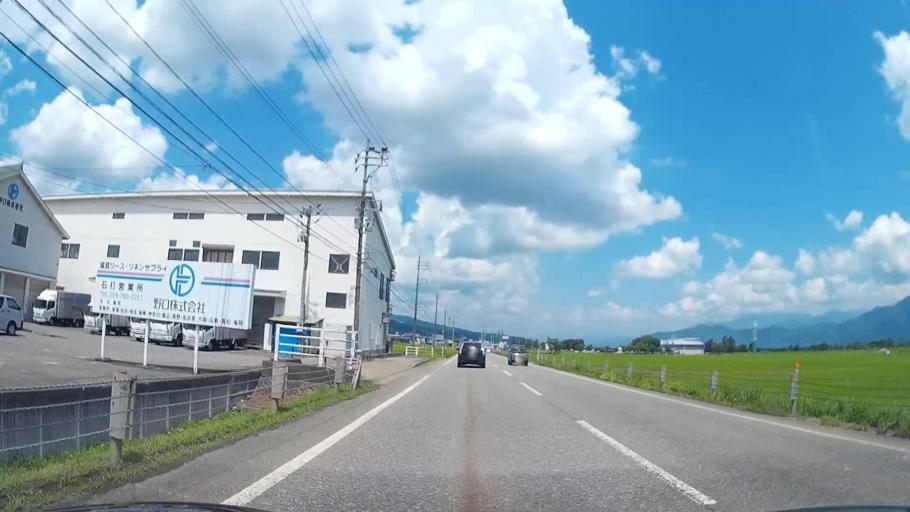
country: JP
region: Niigata
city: Shiozawa
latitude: 36.9995
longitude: 138.8148
